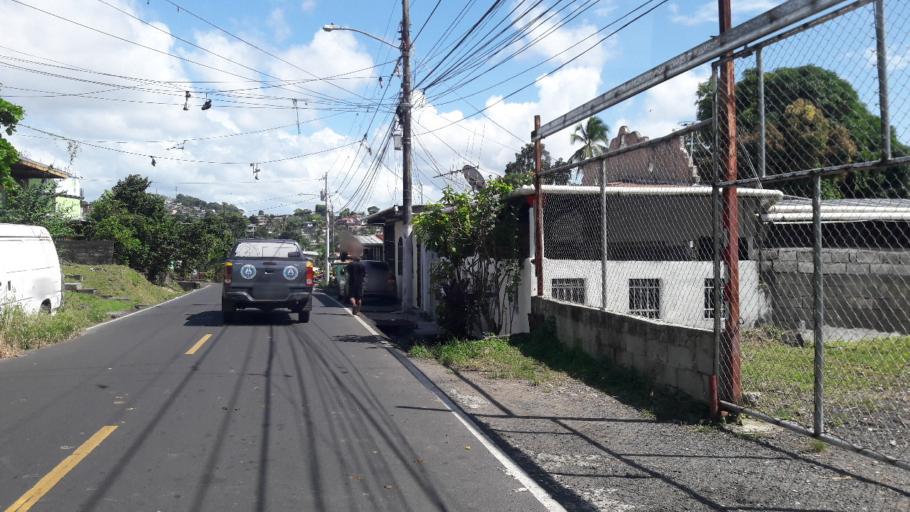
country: PA
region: Panama
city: San Miguelito
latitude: 9.0473
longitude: -79.5037
